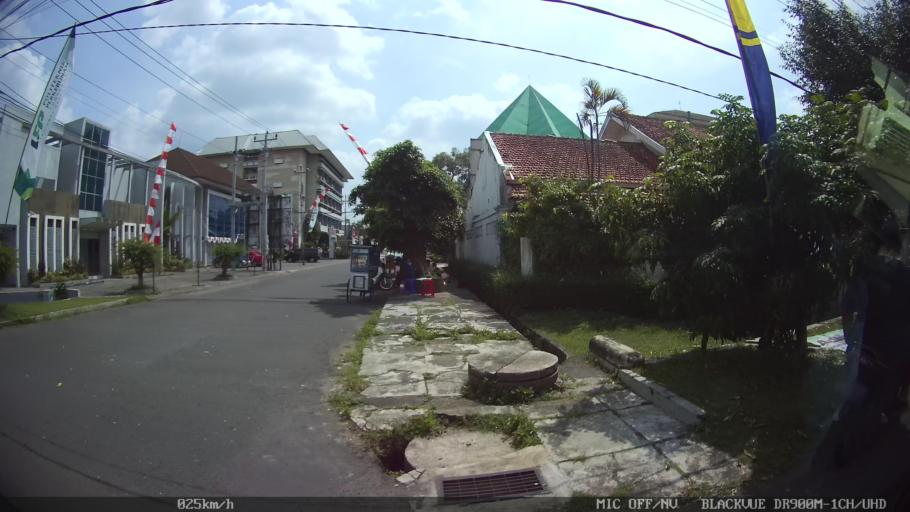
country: ID
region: Daerah Istimewa Yogyakarta
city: Yogyakarta
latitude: -7.7844
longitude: 110.3850
